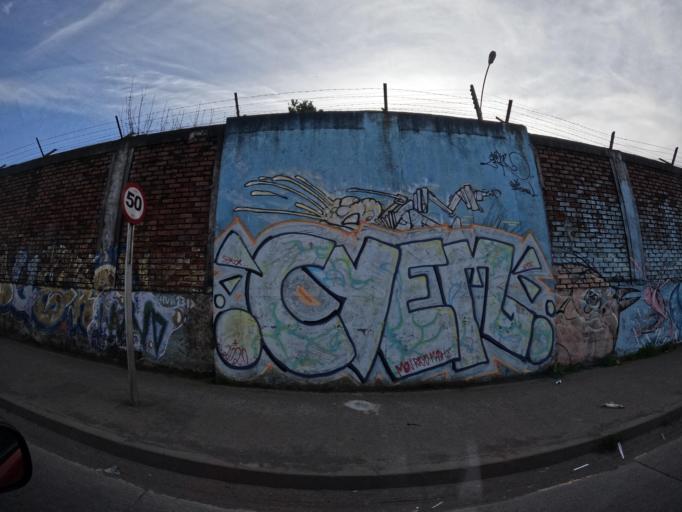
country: CL
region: Biobio
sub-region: Provincia de Concepcion
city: Concepcion
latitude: -36.8015
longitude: -73.0308
